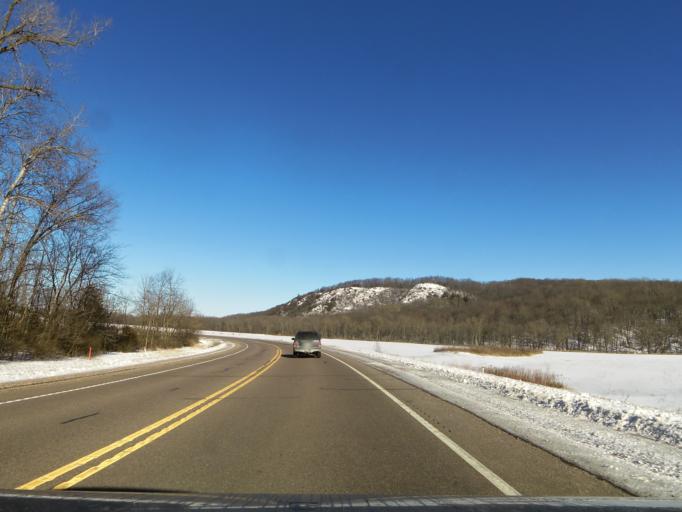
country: US
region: Wisconsin
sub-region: Sauk County
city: Baraboo
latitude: 43.4917
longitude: -89.6348
